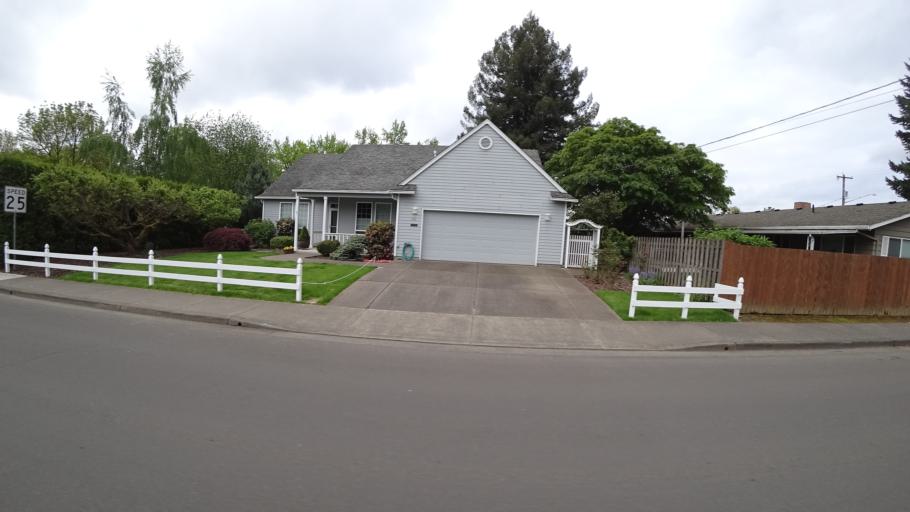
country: US
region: Oregon
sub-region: Washington County
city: Hillsboro
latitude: 45.5443
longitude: -122.9790
